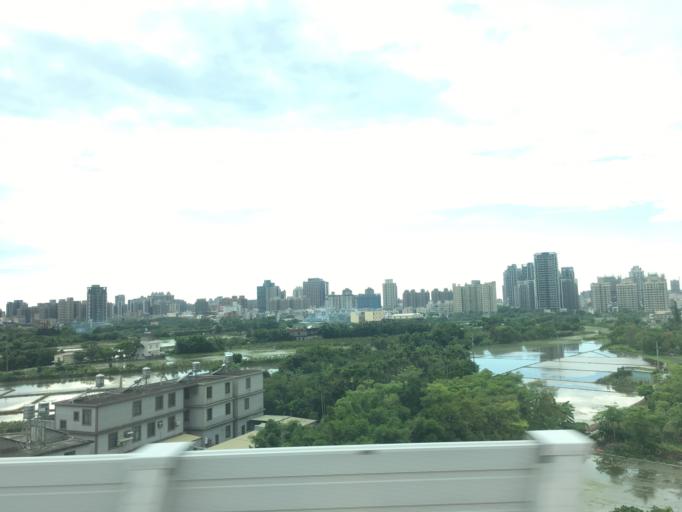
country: TW
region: Taiwan
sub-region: Hsinchu
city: Zhubei
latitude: 24.8179
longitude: 121.0426
